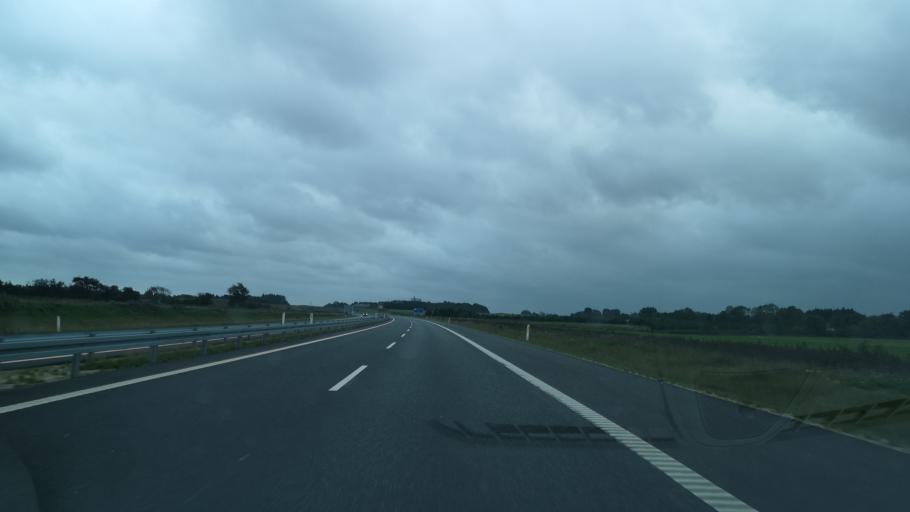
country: DK
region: Central Jutland
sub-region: Herning Kommune
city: Snejbjerg
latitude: 56.1437
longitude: 8.8696
